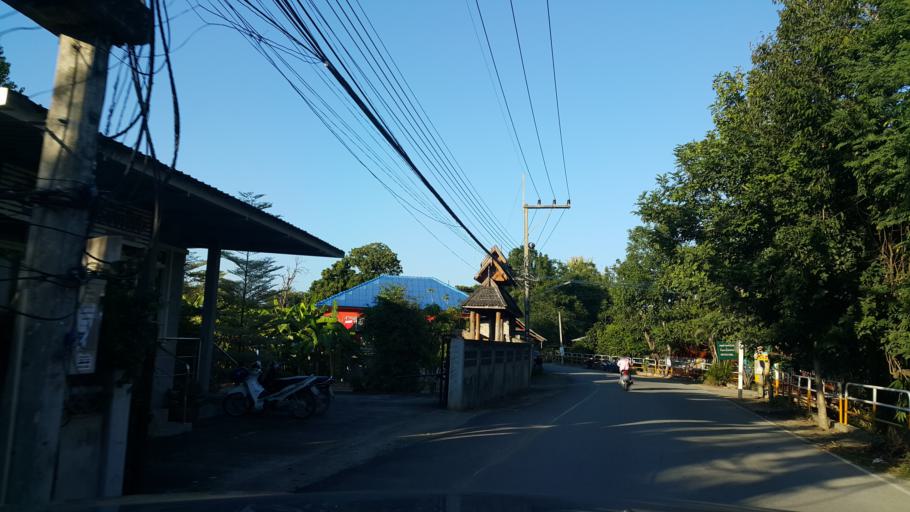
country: TH
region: Chiang Mai
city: Saraphi
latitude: 18.7505
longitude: 99.0489
